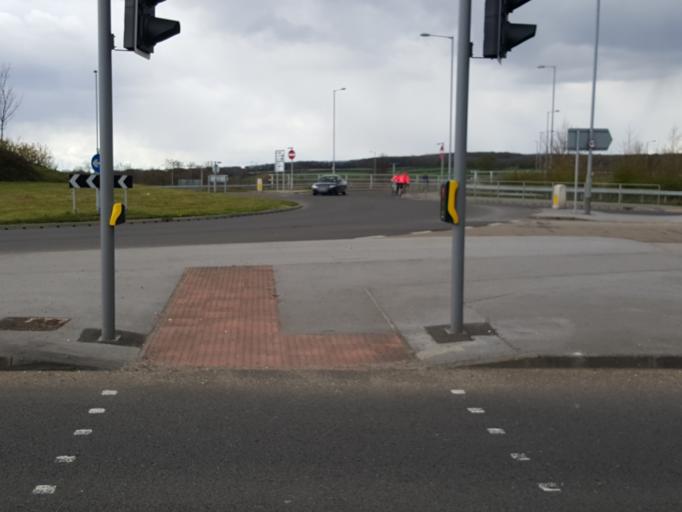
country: GB
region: England
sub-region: East Riding of Yorkshire
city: North Ferriby
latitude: 53.7235
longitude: -0.5193
